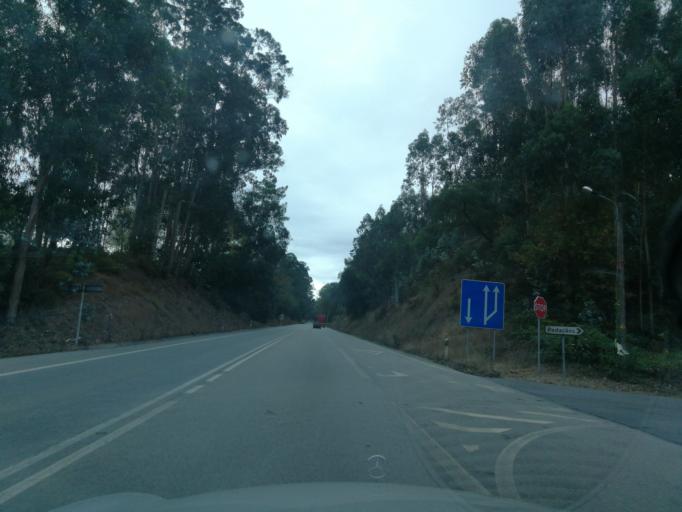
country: PT
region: Aveiro
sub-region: Agueda
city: Valongo
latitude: 40.6309
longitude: -8.4689
